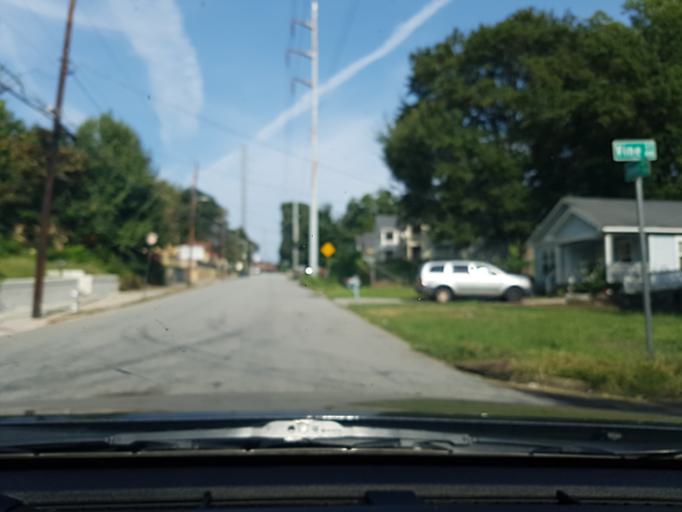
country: US
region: Georgia
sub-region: Fulton County
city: Atlanta
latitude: 33.7643
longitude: -84.4078
